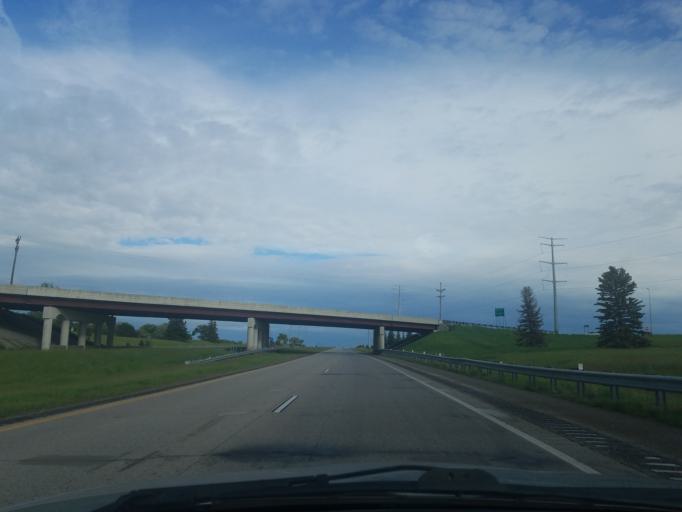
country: US
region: Minnesota
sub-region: Otter Tail County
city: Fergus Falls
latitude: 46.2086
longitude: -96.0205
